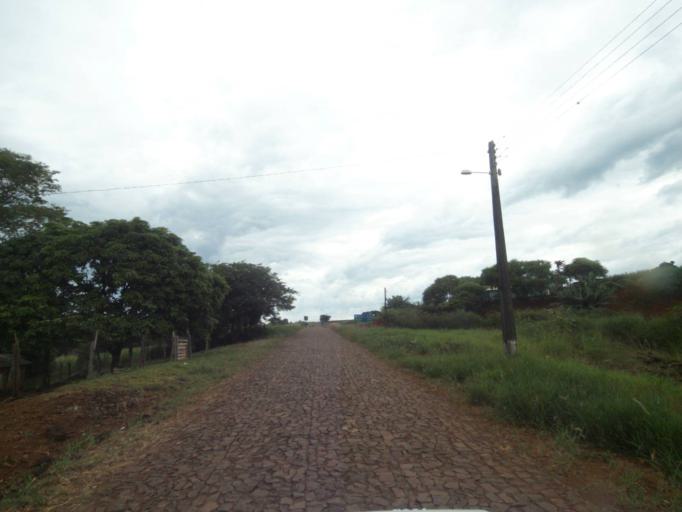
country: BR
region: Parana
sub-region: Guaraniacu
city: Guaraniacu
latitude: -24.9229
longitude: -52.9378
